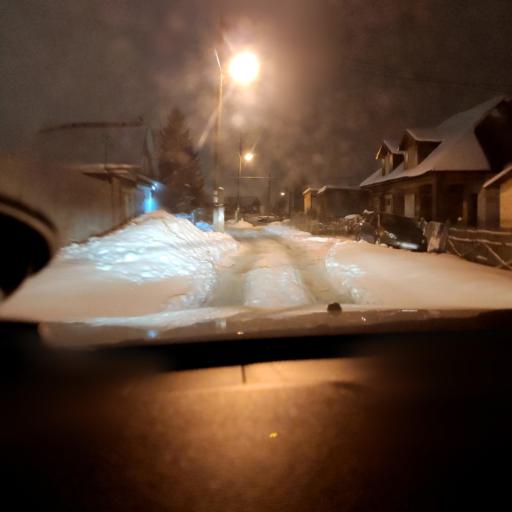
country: RU
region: Samara
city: Petra-Dubrava
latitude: 53.3154
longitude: 50.2990
